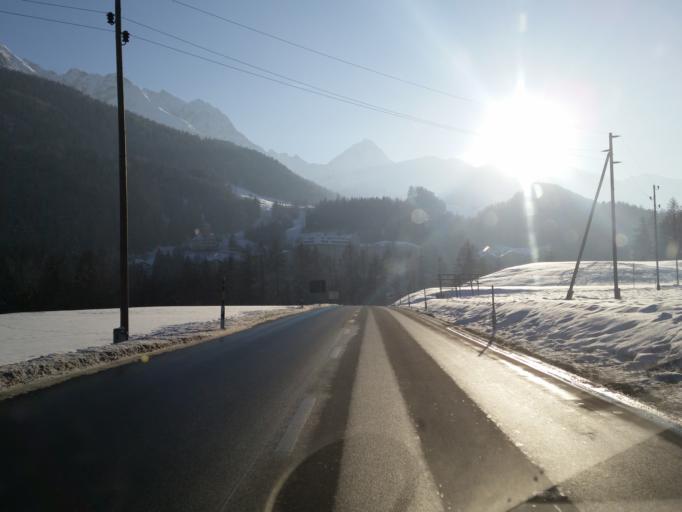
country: CH
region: Grisons
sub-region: Inn District
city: Scuol
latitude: 46.7915
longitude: 10.2880
